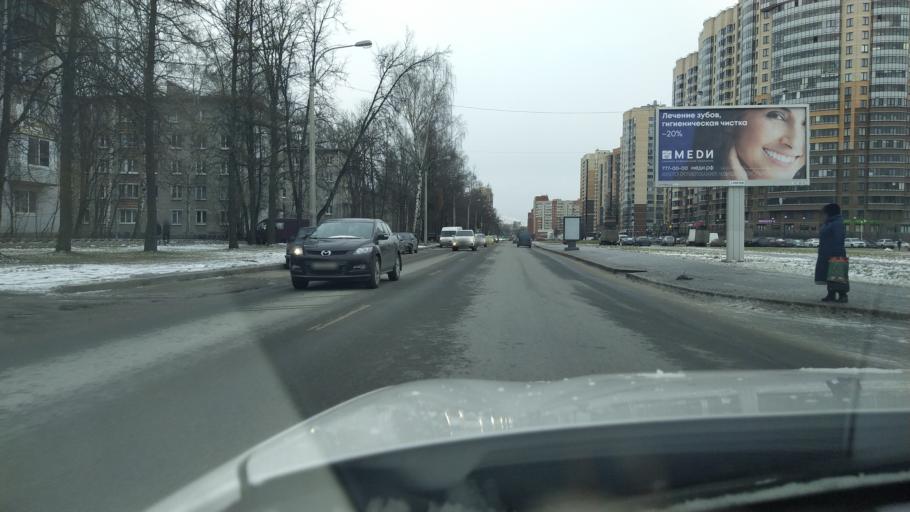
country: RU
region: Leningrad
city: Kalininskiy
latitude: 60.0019
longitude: 30.3967
